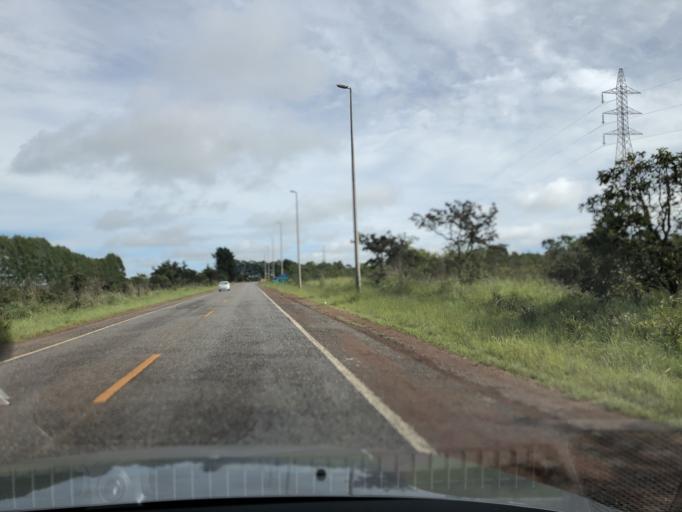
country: BR
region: Federal District
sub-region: Brasilia
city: Brasilia
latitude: -15.6825
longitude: -48.0896
